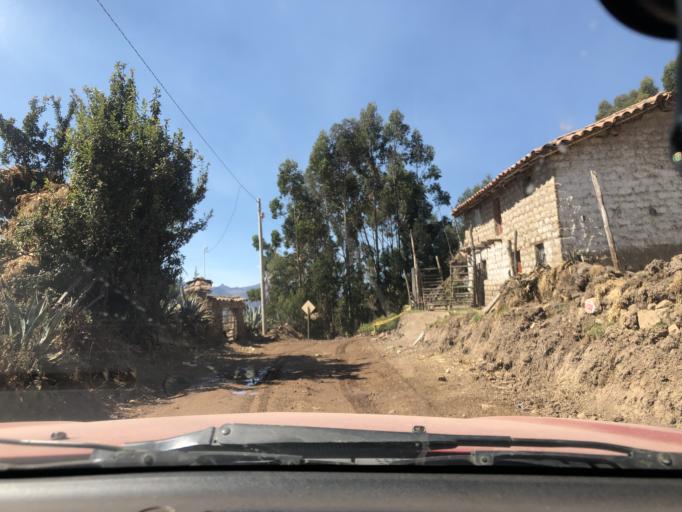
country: PE
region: Ayacucho
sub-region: Provincia de La Mar
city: Chilcas
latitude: -13.1693
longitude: -73.8511
